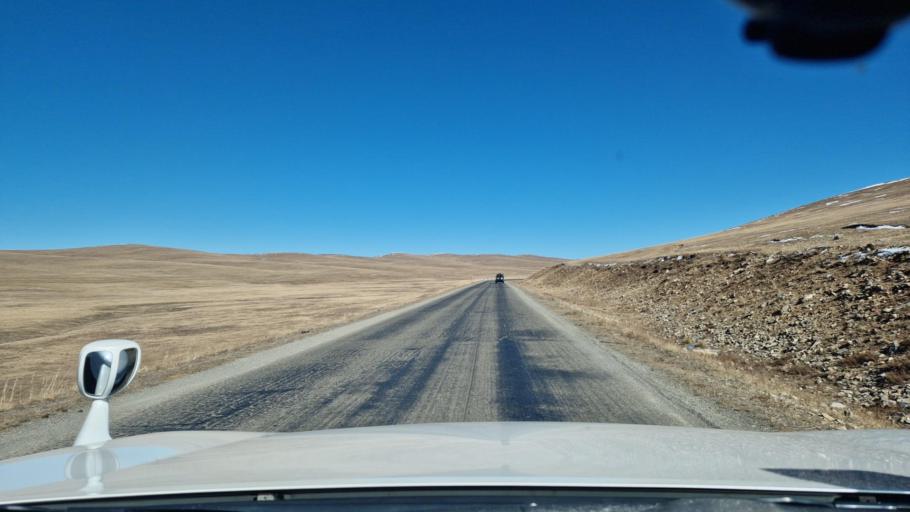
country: MN
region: Hentiy
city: Modot
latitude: 47.7834
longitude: 108.6655
